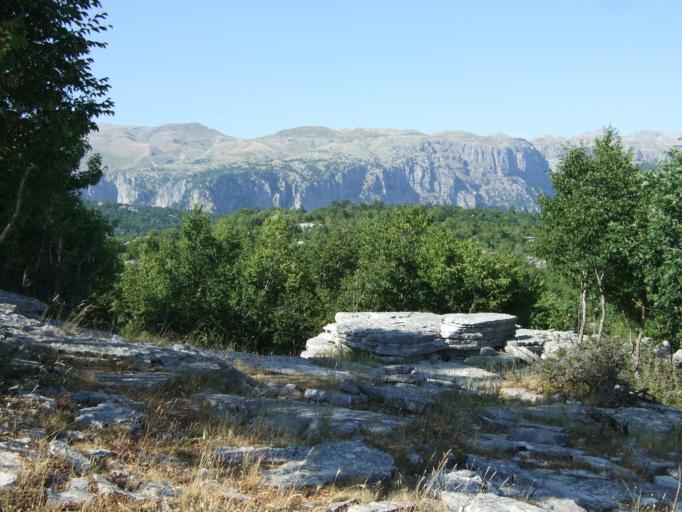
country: GR
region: Epirus
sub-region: Nomos Ioanninon
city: Asprangeloi
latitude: 39.8942
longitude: 20.7431
